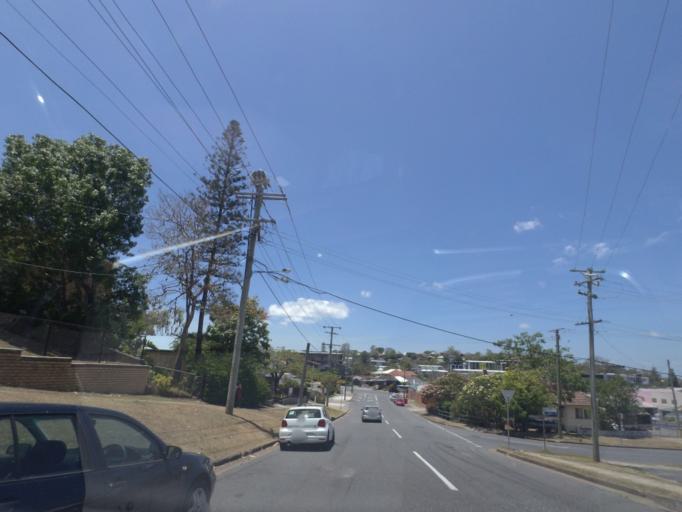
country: AU
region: Queensland
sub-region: Brisbane
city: Mount Gravatt East
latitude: -27.5375
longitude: 153.0768
